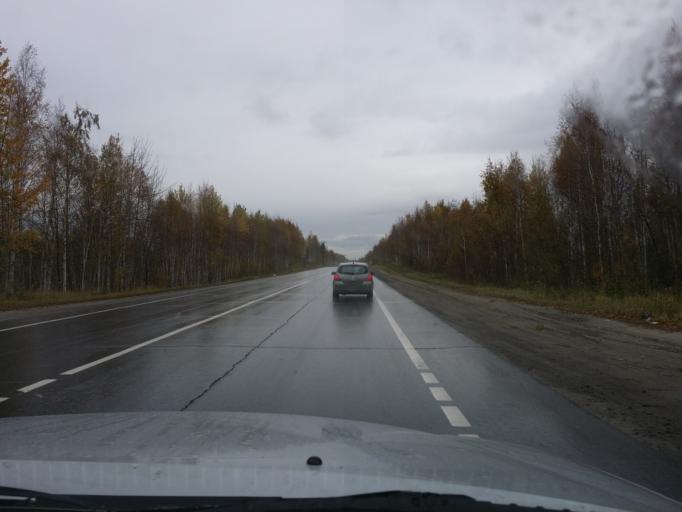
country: RU
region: Khanty-Mansiyskiy Avtonomnyy Okrug
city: Megion
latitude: 61.0634
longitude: 76.1152
